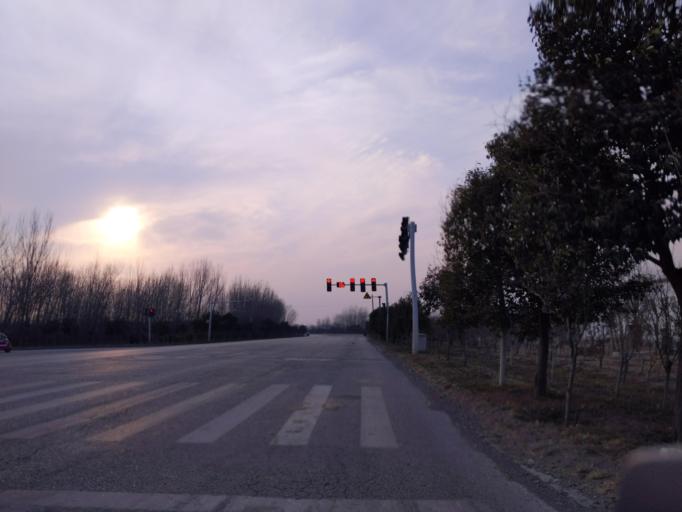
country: CN
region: Henan Sheng
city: Puyang
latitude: 35.8201
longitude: 114.9814
